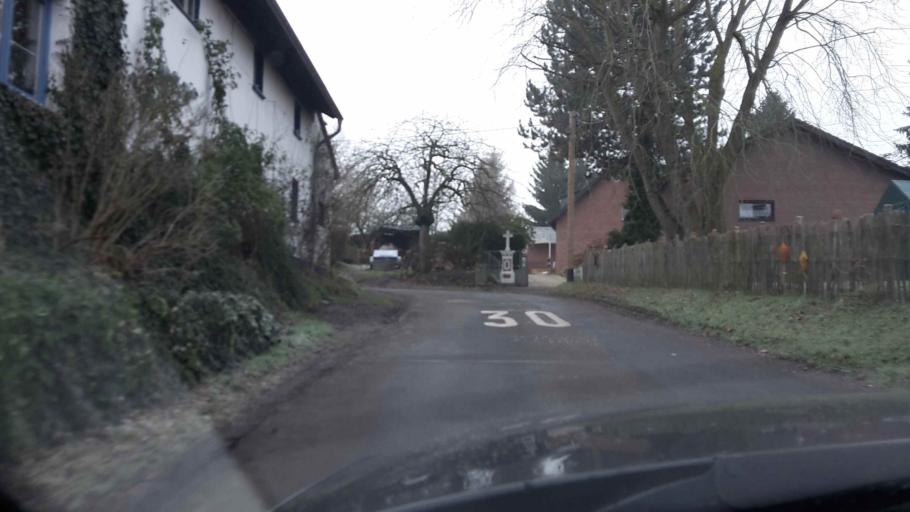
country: DE
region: North Rhine-Westphalia
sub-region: Regierungsbezirk Koln
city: Hennef
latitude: 50.7201
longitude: 7.3019
